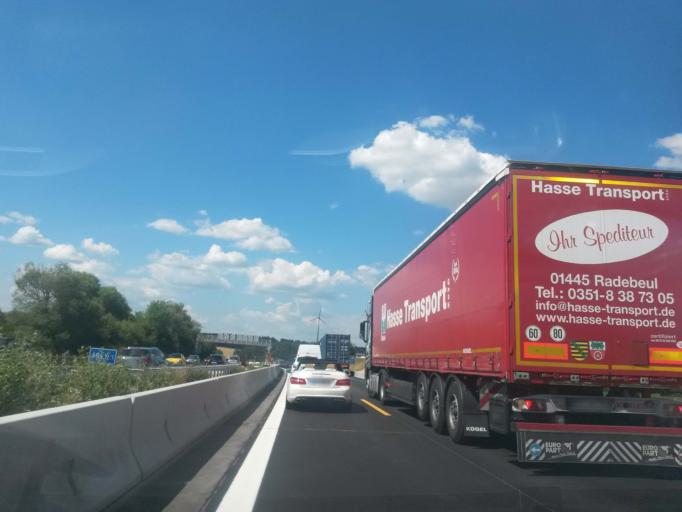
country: DE
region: Bavaria
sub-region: Upper Bavaria
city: Allershausen
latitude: 48.4555
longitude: 11.5908
